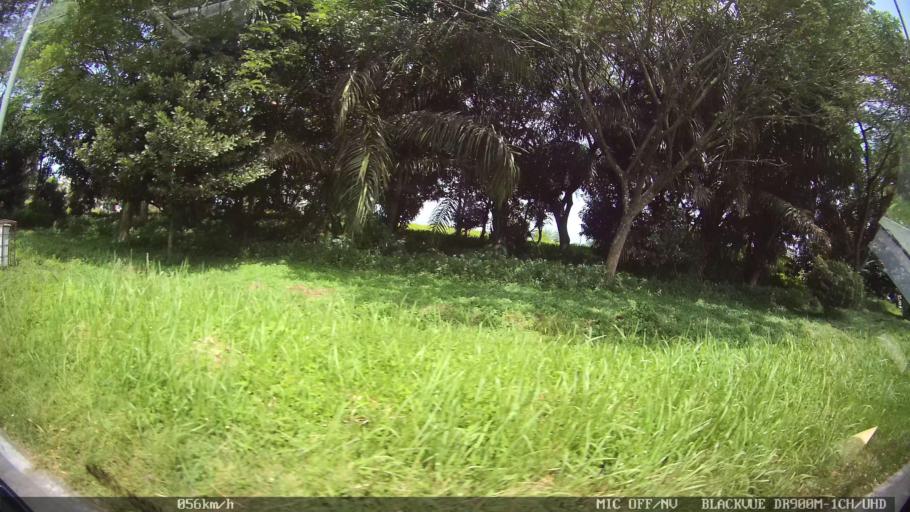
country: ID
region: North Sumatra
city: Percut
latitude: 3.6259
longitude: 98.8671
